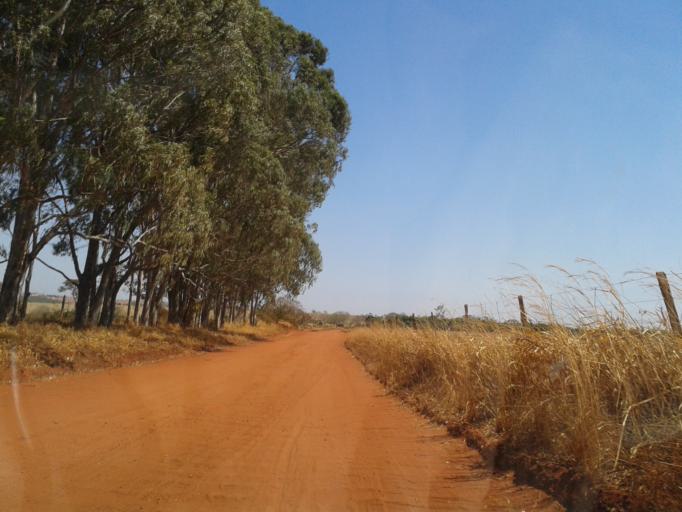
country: BR
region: Minas Gerais
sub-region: Ituiutaba
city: Ituiutaba
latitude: -18.9924
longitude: -49.3817
